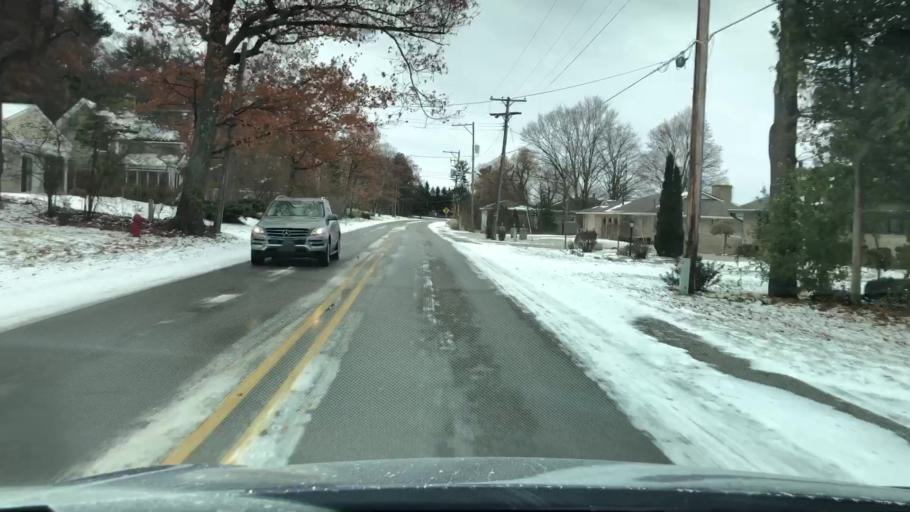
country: US
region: Michigan
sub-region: Grand Traverse County
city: Traverse City
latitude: 44.7882
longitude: -85.5880
